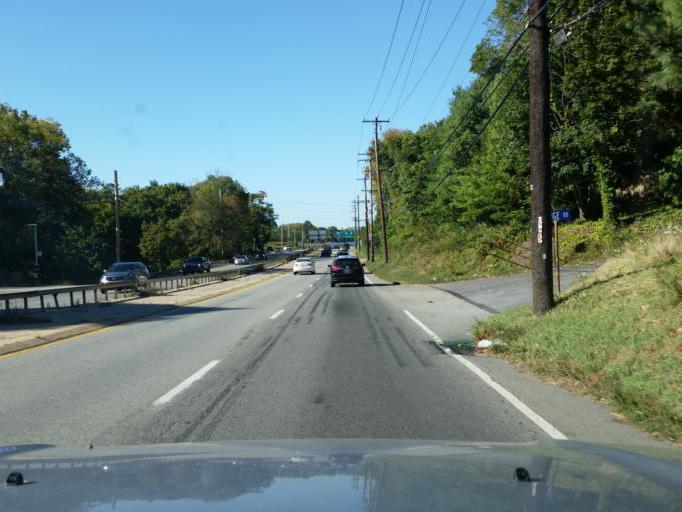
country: US
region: Pennsylvania
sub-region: Chester County
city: West Chester
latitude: 39.9355
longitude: -75.5886
